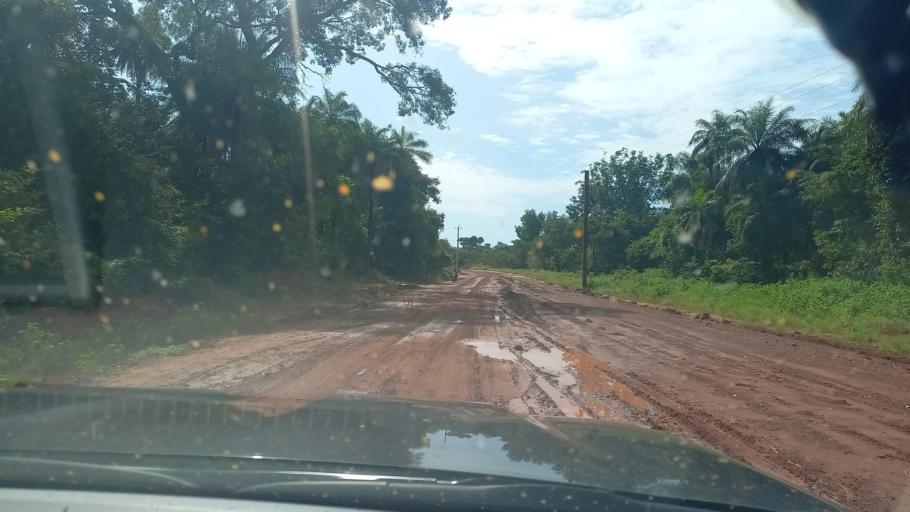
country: SN
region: Ziguinchor
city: Ziguinchor
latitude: 12.6721
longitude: -16.1905
